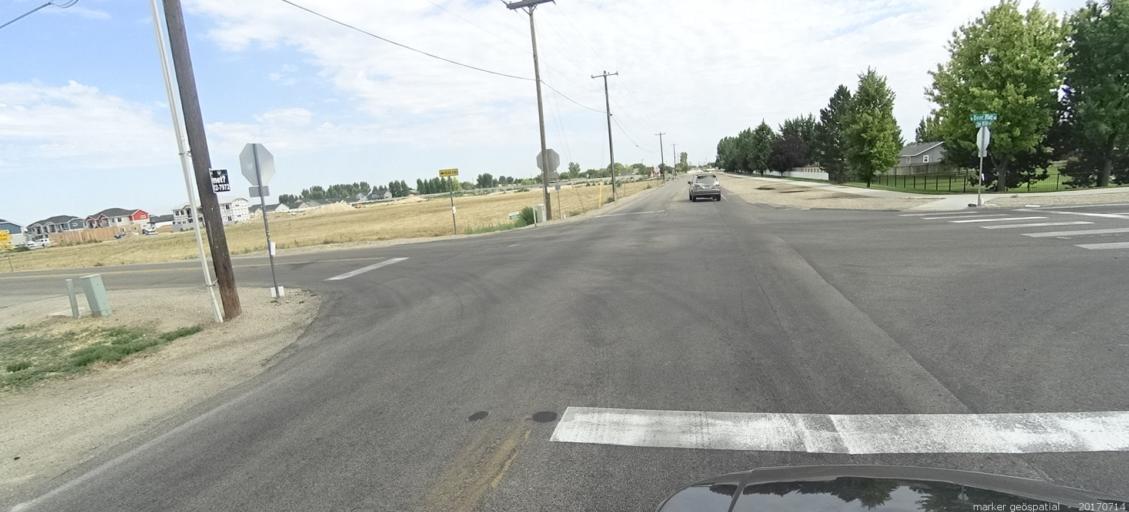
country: US
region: Idaho
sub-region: Ada County
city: Kuna
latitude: 43.5027
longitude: -116.4337
